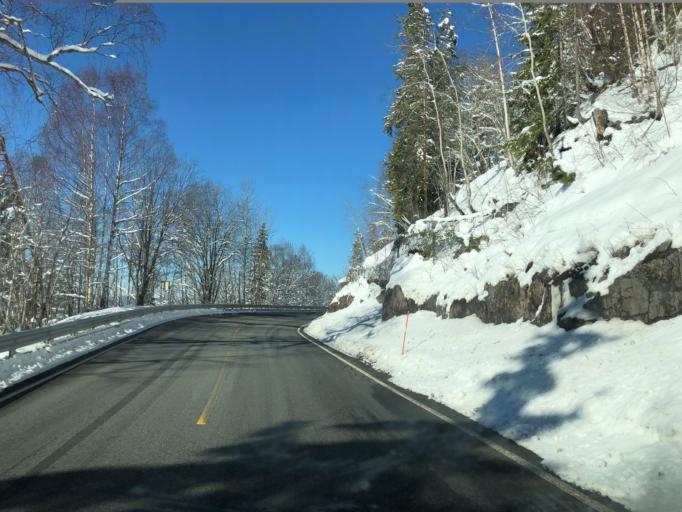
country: NO
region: Akershus
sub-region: Baerum
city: Skui
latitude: 59.9441
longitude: 10.3381
